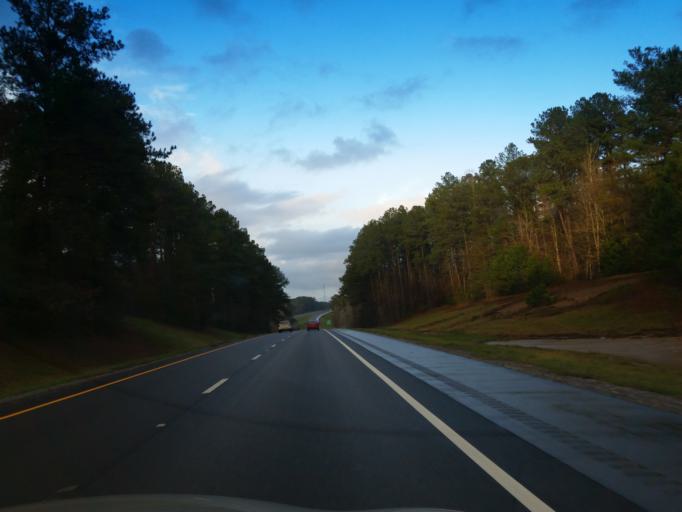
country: US
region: Mississippi
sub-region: Jones County
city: Sharon
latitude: 31.9525
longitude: -88.9788
